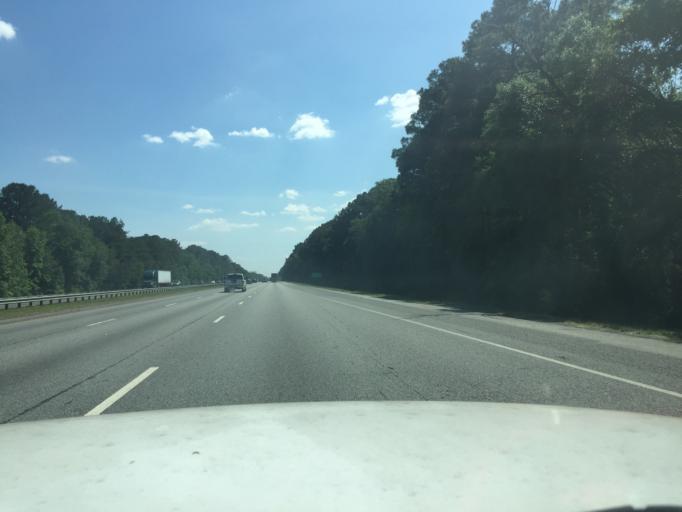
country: US
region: Georgia
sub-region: Chatham County
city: Pooler
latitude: 32.0688
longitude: -81.2489
